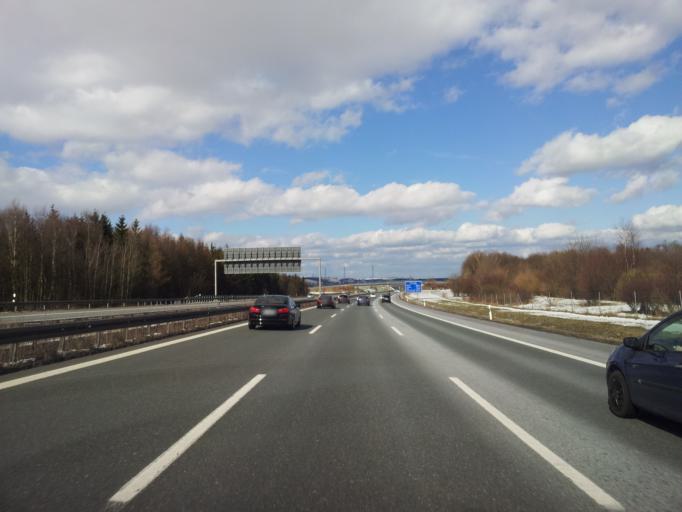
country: DE
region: Bavaria
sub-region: Upper Franconia
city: Munchberg
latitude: 50.1738
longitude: 11.7486
